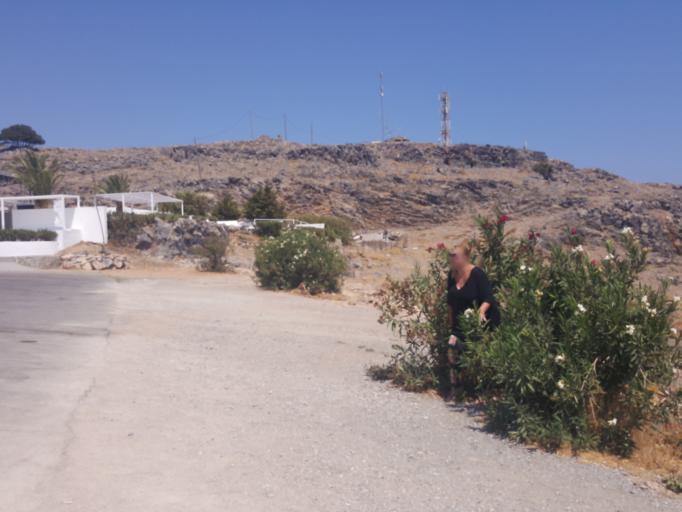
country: GR
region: South Aegean
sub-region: Nomos Dodekanisou
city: Lardos
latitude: 36.1003
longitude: 28.0804
